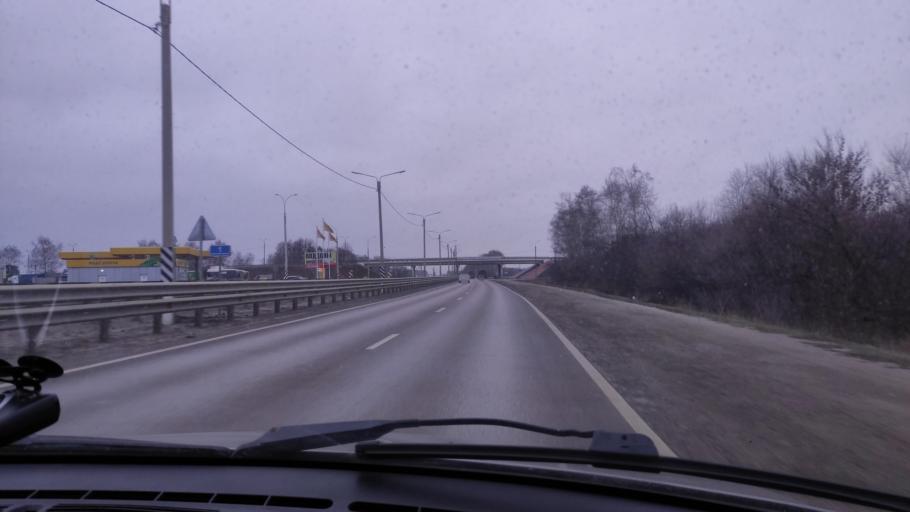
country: RU
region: Tambov
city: Komsomolets
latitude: 52.7331
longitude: 41.2997
